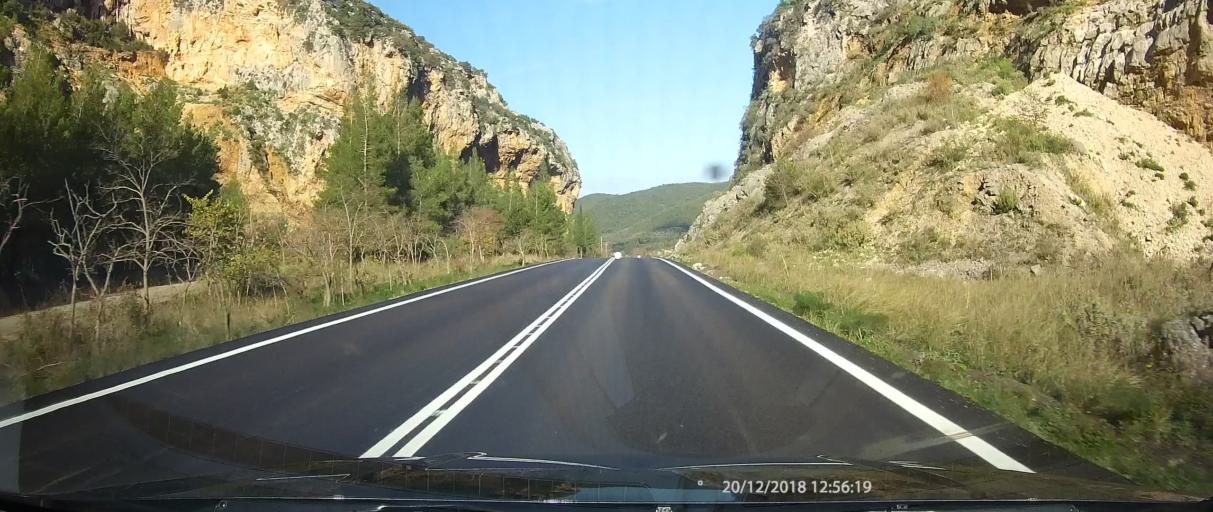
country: GR
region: West Greece
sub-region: Nomos Aitolias kai Akarnanias
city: Pappadhatai
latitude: 38.5089
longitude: 21.3788
